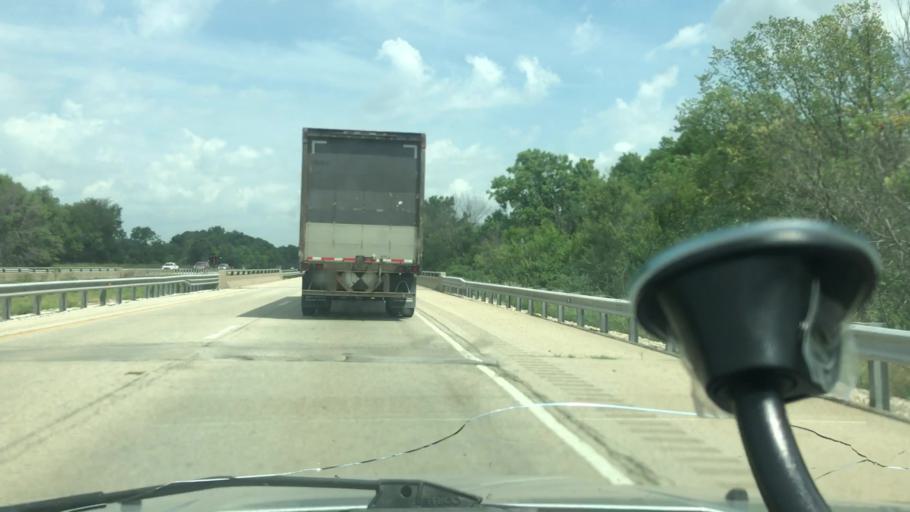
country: US
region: Illinois
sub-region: Peoria County
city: Bellevue
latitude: 40.7177
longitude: -89.6762
